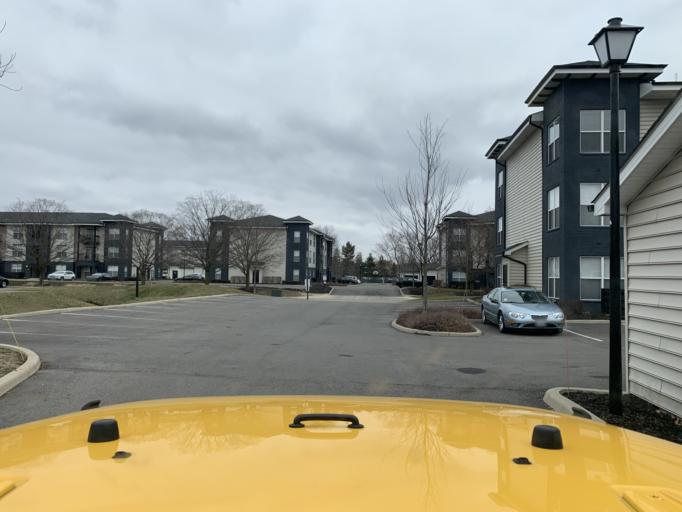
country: US
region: Ohio
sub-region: Franklin County
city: Dublin
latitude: 40.1052
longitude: -83.0813
